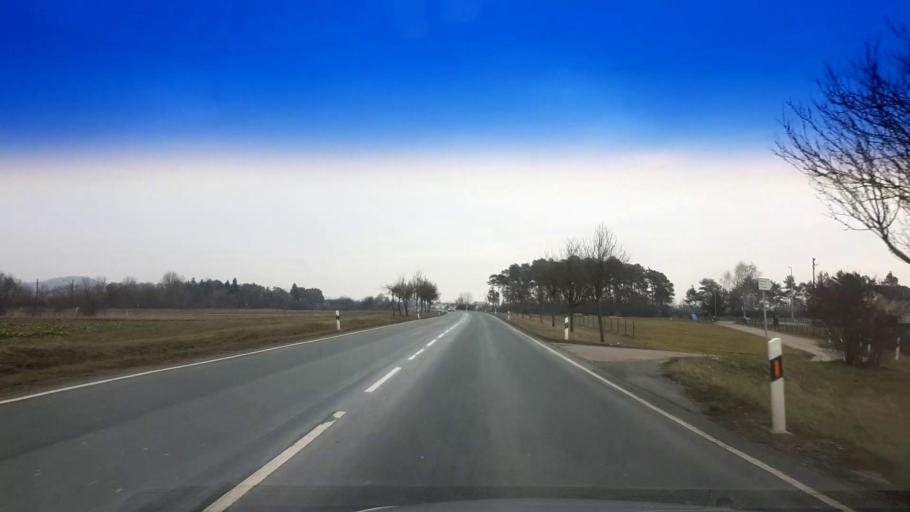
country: DE
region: Bavaria
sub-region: Upper Franconia
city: Hirschaid
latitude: 49.8101
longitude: 10.9994
